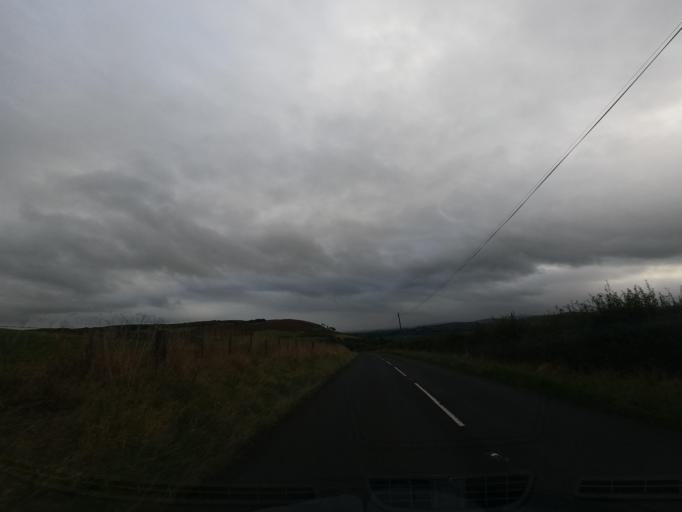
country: GB
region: England
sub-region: Northumberland
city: Doddington
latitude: 55.5956
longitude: -2.0030
